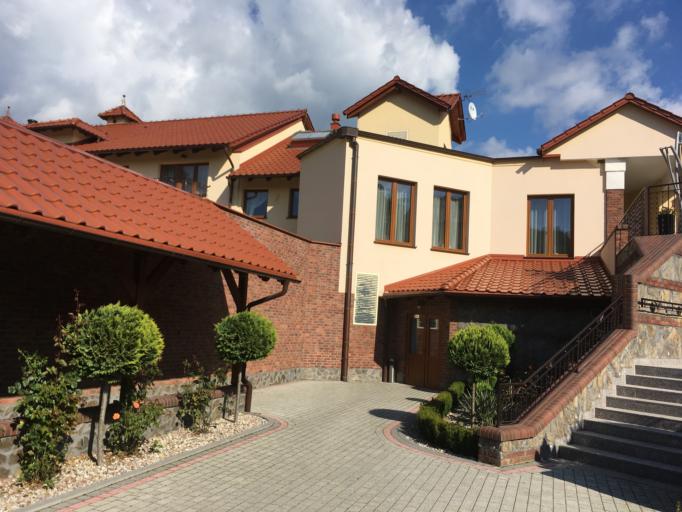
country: PL
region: Kujawsko-Pomorskie
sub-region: Powiat swiecki
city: Osie
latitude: 53.6200
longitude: 18.2584
